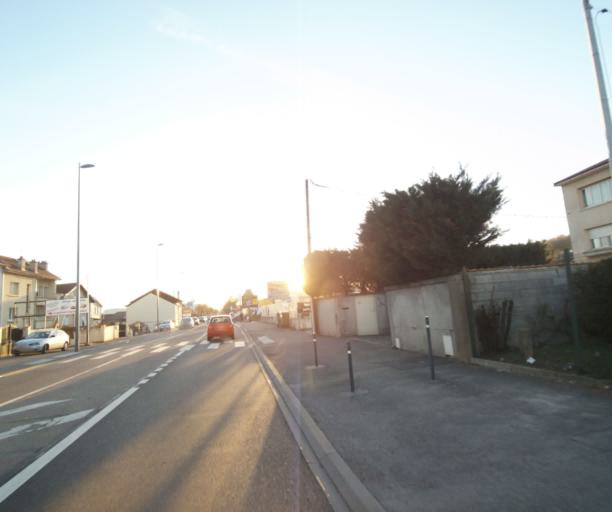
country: FR
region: Lorraine
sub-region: Departement de Meurthe-et-Moselle
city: Essey-les-Nancy
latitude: 48.7092
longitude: 6.2394
